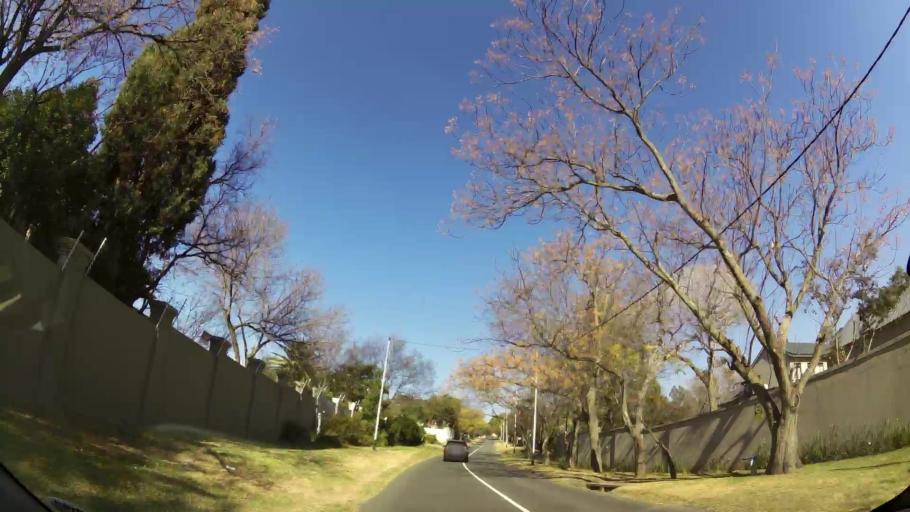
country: ZA
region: Gauteng
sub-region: City of Johannesburg Metropolitan Municipality
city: Midrand
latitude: -26.0478
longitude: 28.0397
